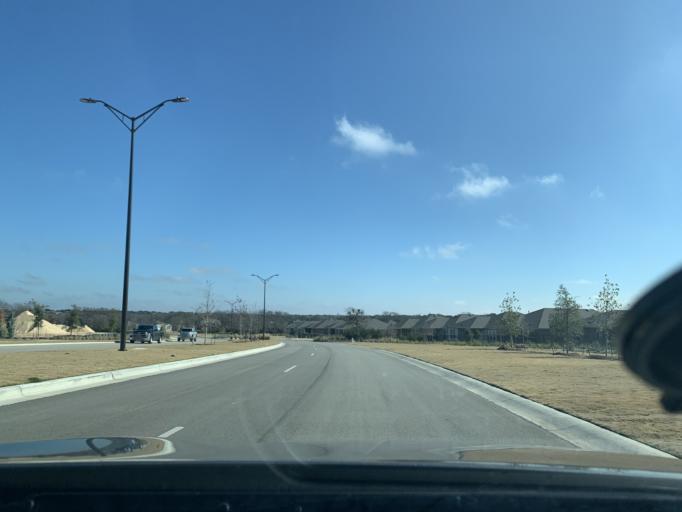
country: US
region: Texas
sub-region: Williamson County
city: Serenada
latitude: 30.7312
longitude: -97.7591
